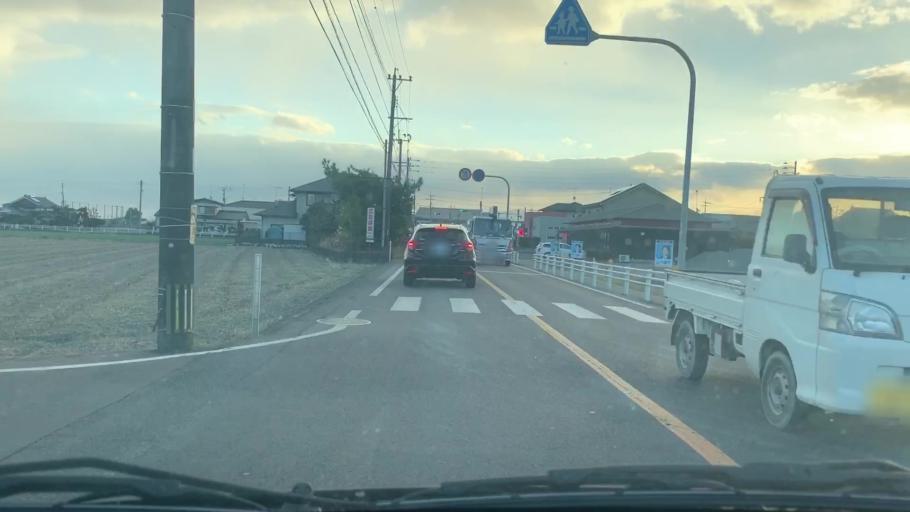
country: JP
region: Saga Prefecture
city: Saga-shi
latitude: 33.1866
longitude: 130.1929
